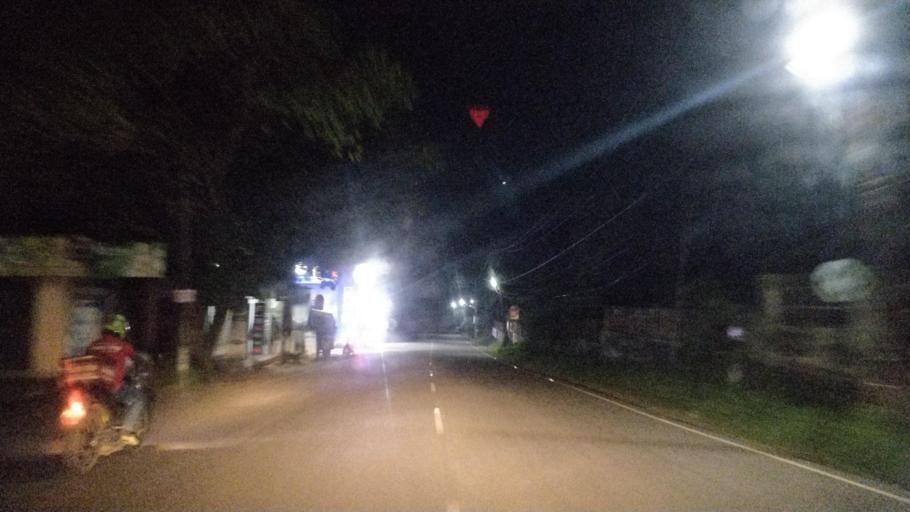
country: IN
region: Kerala
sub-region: Kottayam
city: Kottayam
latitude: 9.6308
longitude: 76.5187
